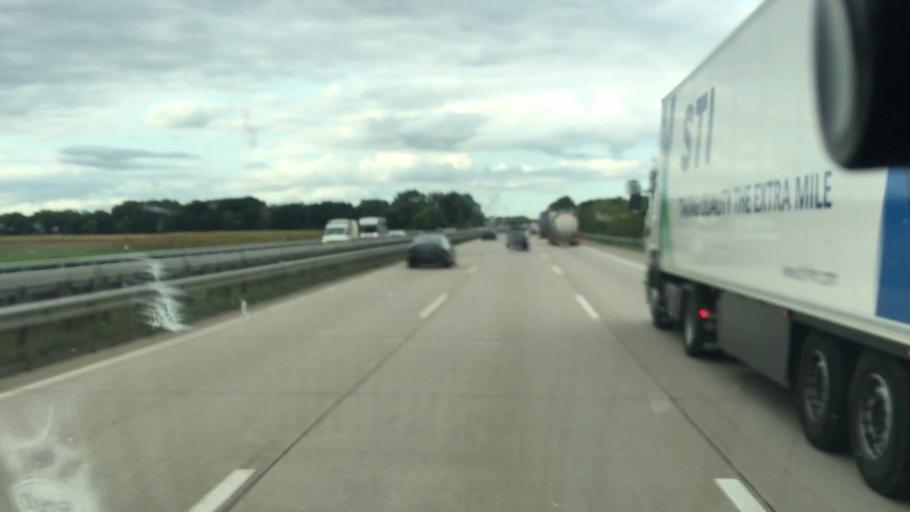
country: DE
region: Lower Saxony
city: Bakum
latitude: 52.7545
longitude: 8.1826
